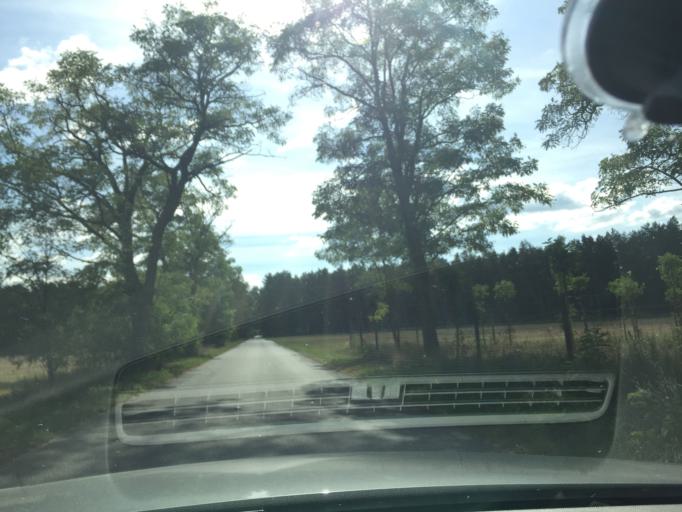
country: DE
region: Brandenburg
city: Spreenhagen
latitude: 52.3617
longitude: 13.8780
